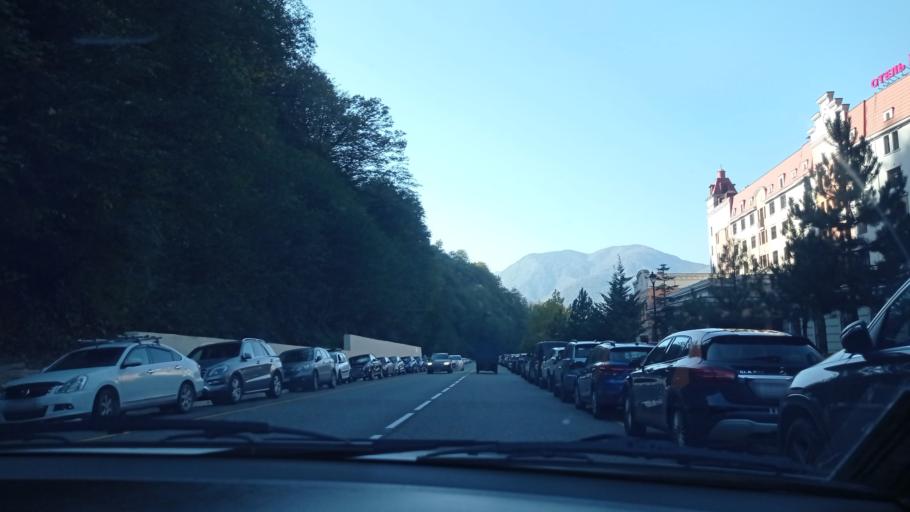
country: RU
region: Krasnodarskiy
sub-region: Sochi City
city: Krasnaya Polyana
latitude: 43.6713
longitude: 40.2937
